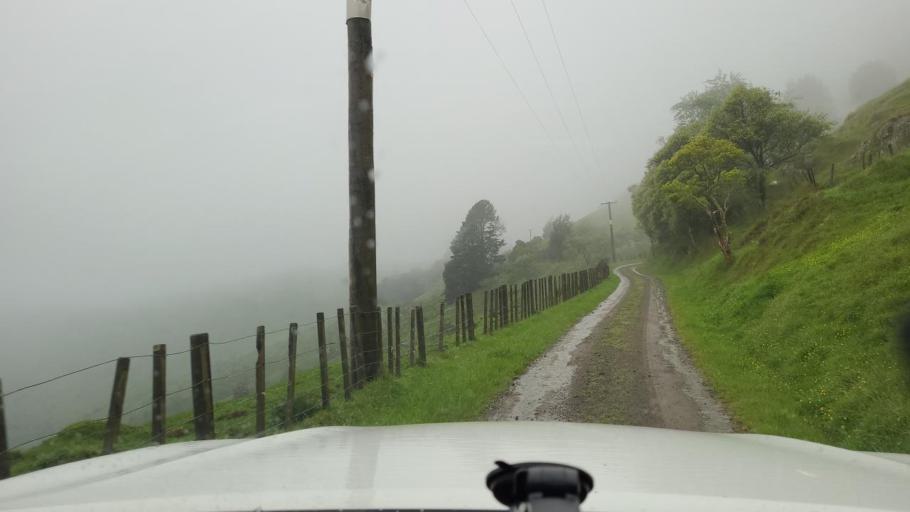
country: NZ
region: Gisborne
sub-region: Gisborne District
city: Gisborne
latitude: -38.4853
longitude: 177.6174
